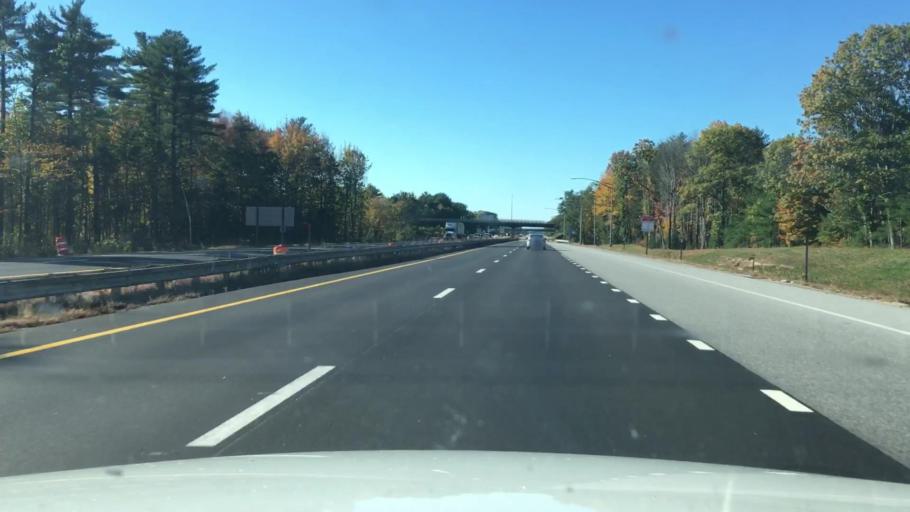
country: US
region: Maine
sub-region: Cumberland County
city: South Portland Gardens
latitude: 43.6280
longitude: -70.3487
